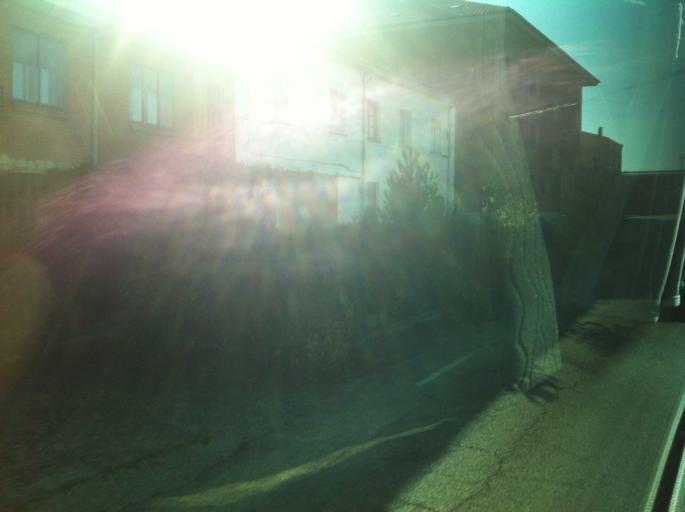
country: ES
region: Castille and Leon
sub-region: Provincia de Burgos
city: Lerma
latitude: 42.0241
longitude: -3.7650
